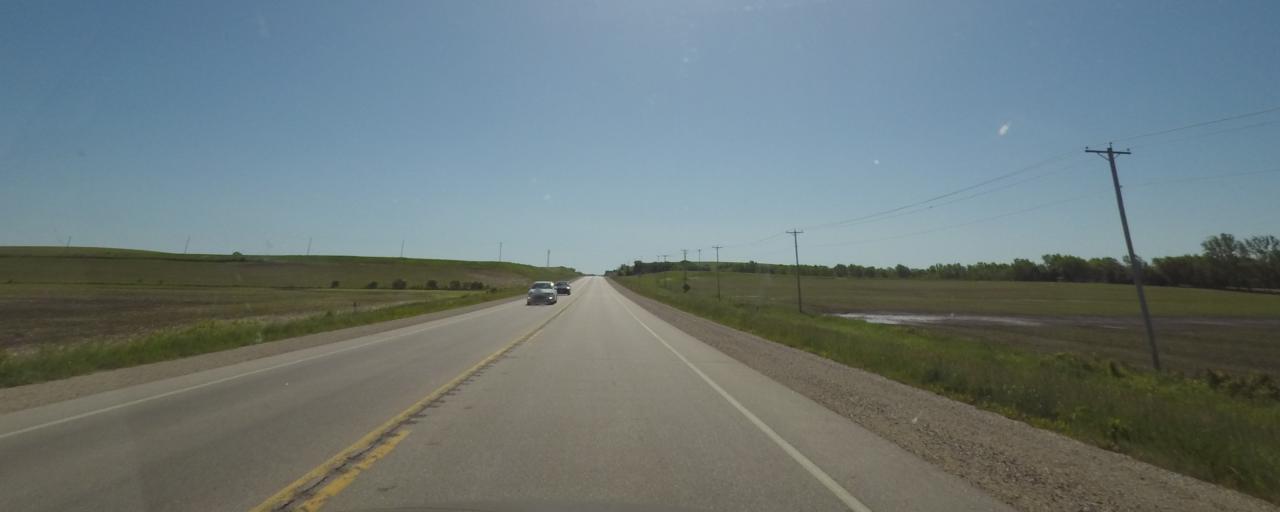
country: US
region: Wisconsin
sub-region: Fond du Lac County
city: Saint Peter
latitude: 43.7833
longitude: -88.3264
